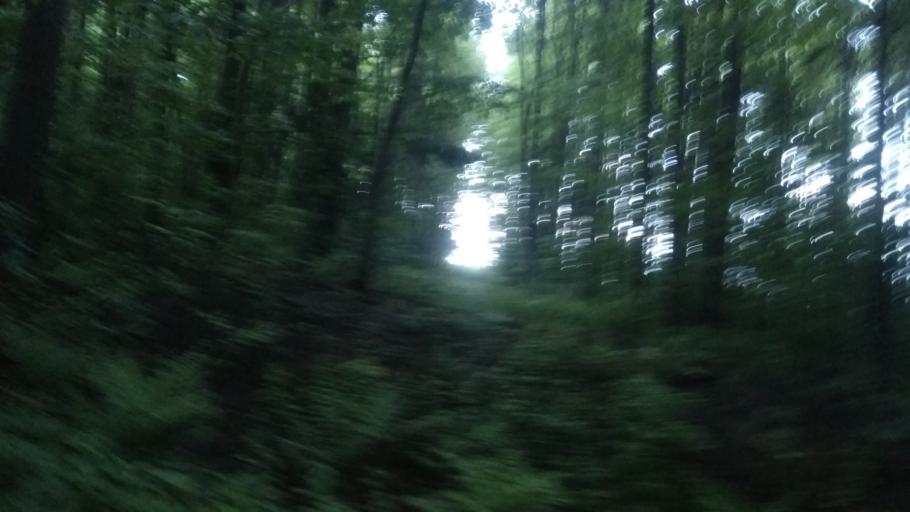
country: RU
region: Perm
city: Ferma
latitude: 57.9670
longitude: 56.3461
